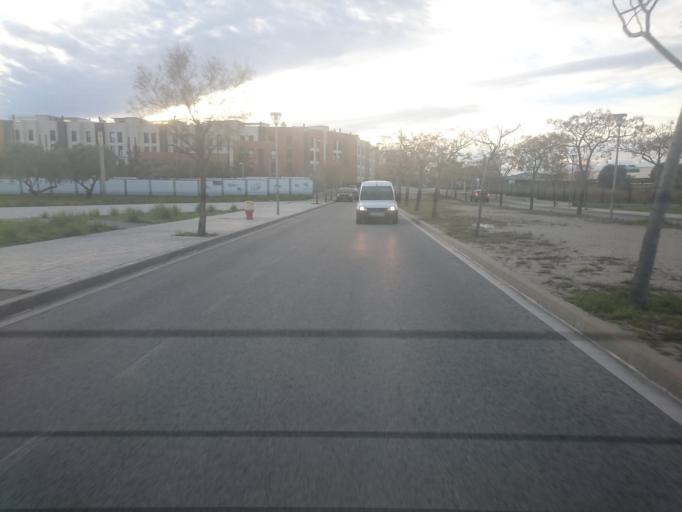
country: ES
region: Catalonia
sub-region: Provincia de Tarragona
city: Cunit
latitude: 41.1981
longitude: 1.6555
